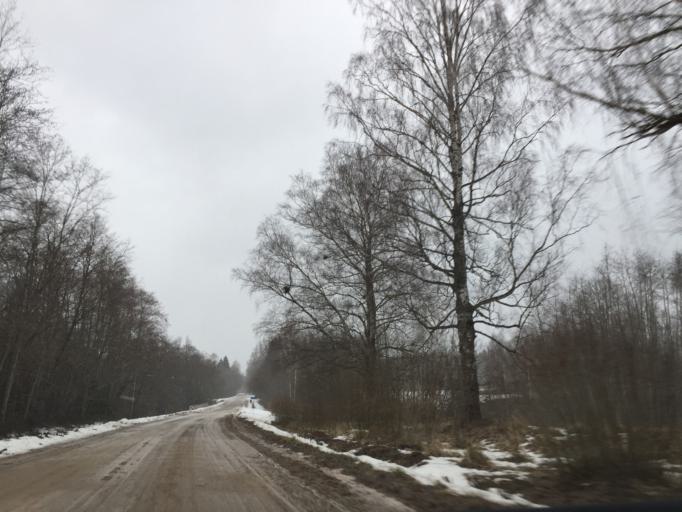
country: LV
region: Salacgrivas
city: Salacgriva
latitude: 57.6500
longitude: 24.4681
